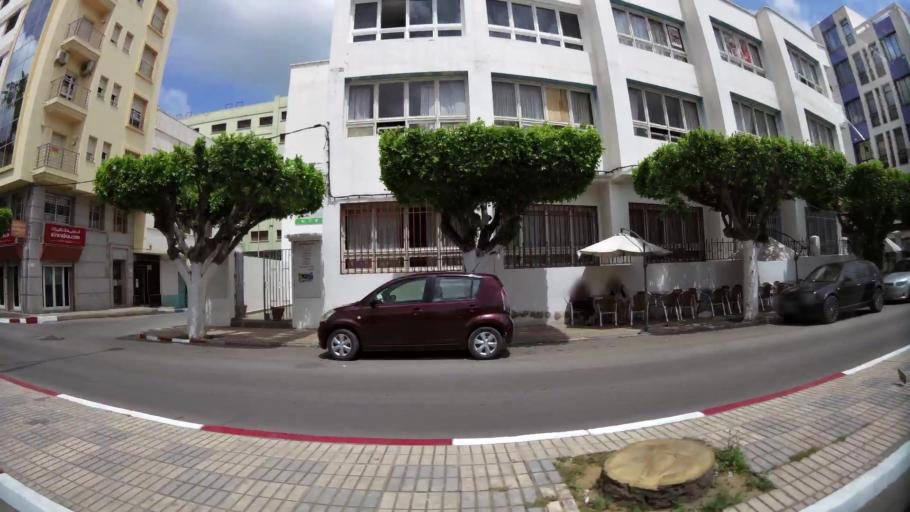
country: MA
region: Oriental
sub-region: Nador
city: Nador
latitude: 35.1808
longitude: -2.9263
